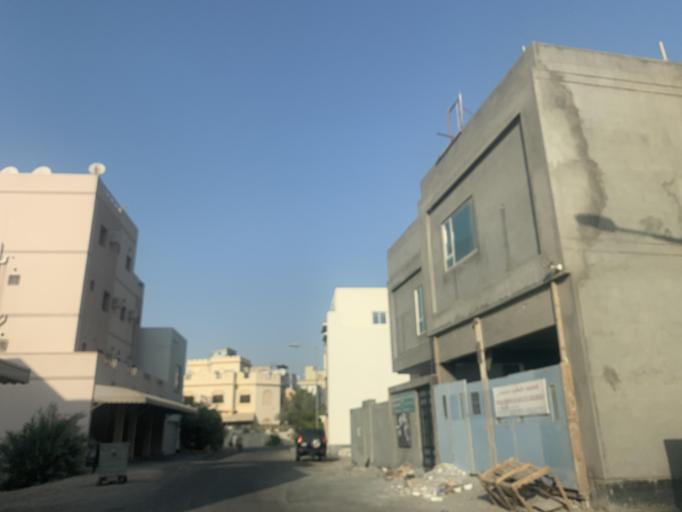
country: BH
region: Manama
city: Jidd Hafs
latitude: 26.2167
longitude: 50.5243
